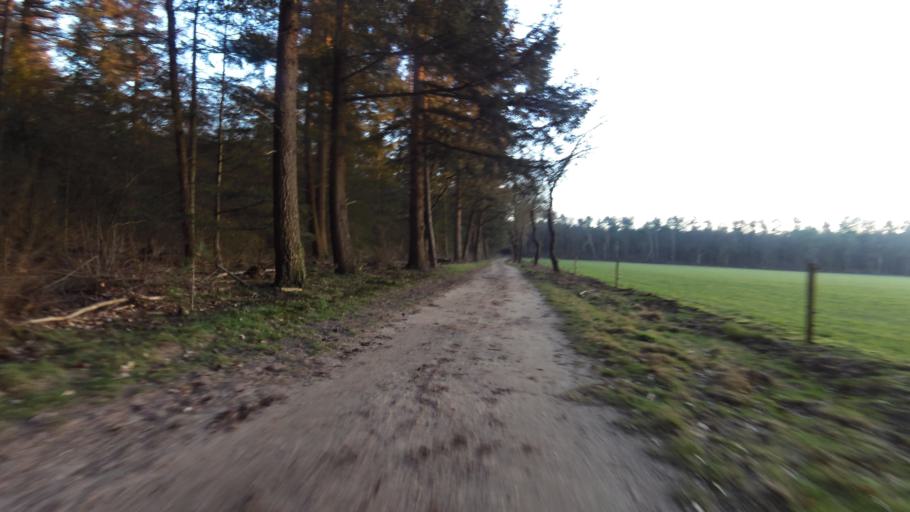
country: NL
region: Gelderland
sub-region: Gemeente Barneveld
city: Garderen
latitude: 52.2299
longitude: 5.6820
